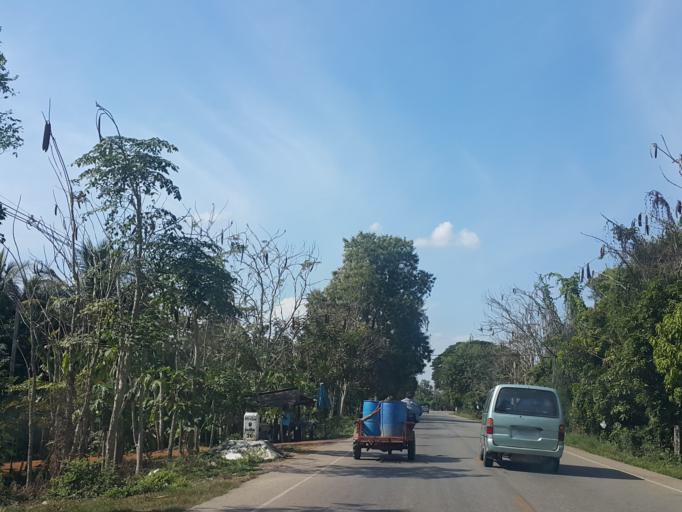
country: TH
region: Sukhothai
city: Sawankhalok
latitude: 17.2562
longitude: 99.8397
